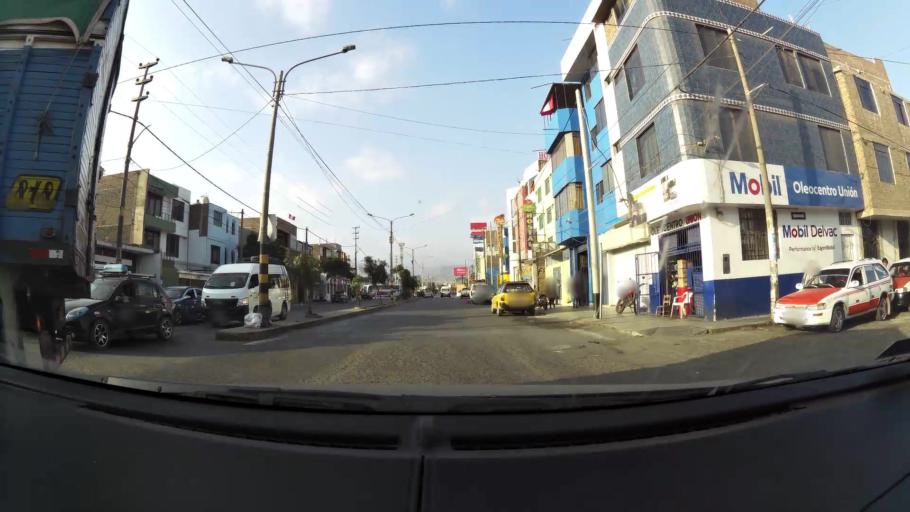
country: PE
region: La Libertad
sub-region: Provincia de Trujillo
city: El Porvenir
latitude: -8.0919
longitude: -79.0076
